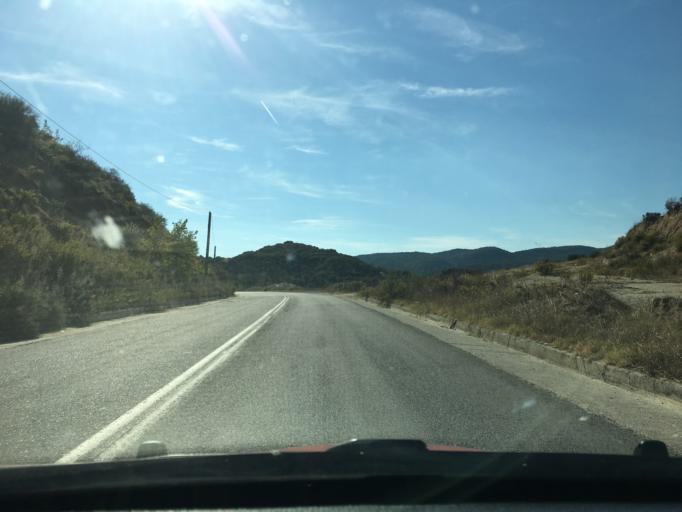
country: GR
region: Central Macedonia
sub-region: Nomos Chalkidikis
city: Ierissos
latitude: 40.3909
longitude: 23.8636
